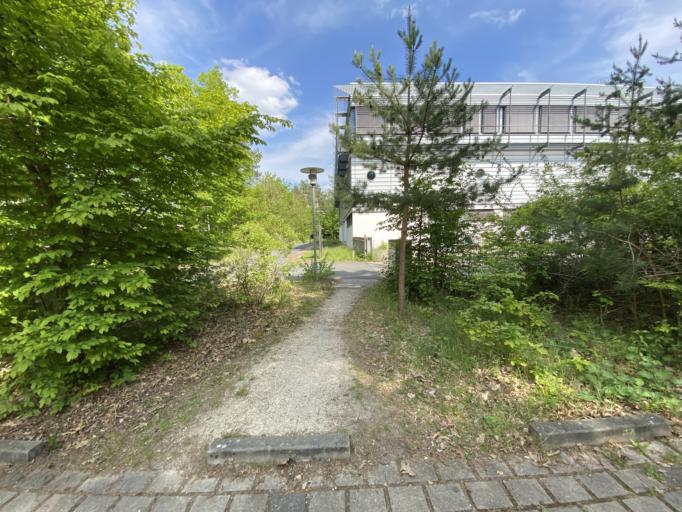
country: DE
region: Bavaria
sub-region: Regierungsbezirk Mittelfranken
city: Erlangen
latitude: 49.5799
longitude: 11.0271
